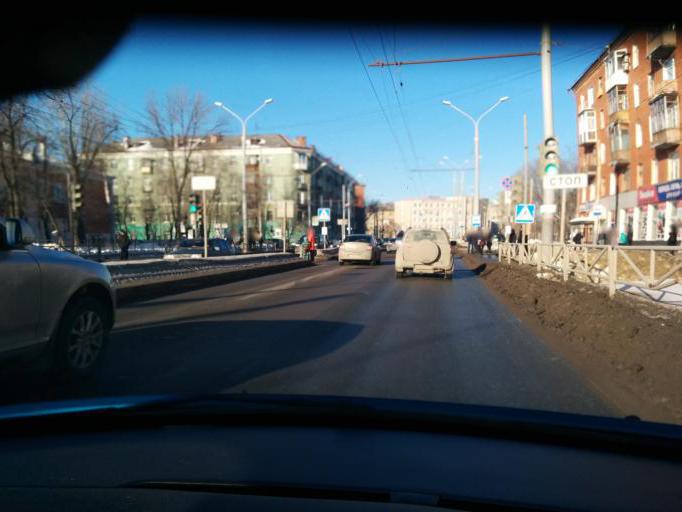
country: RU
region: Perm
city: Perm
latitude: 57.9902
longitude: 56.2574
